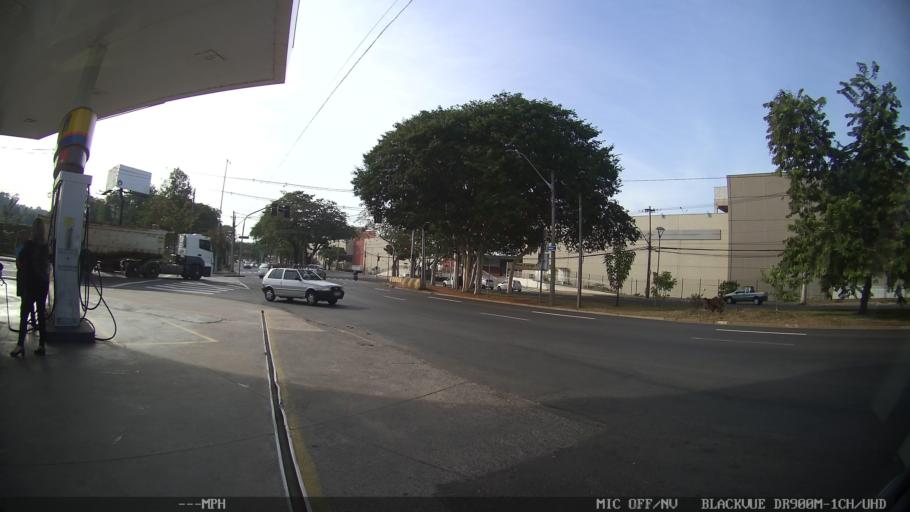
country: BR
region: Sao Paulo
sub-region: Piracicaba
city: Piracicaba
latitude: -22.7029
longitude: -47.6510
